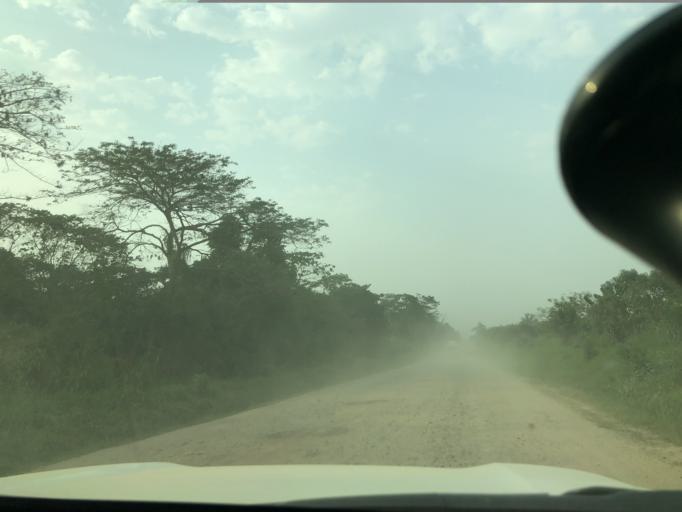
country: UG
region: Western Region
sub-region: Kasese District
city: Margherita
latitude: 0.2663
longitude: 29.6760
